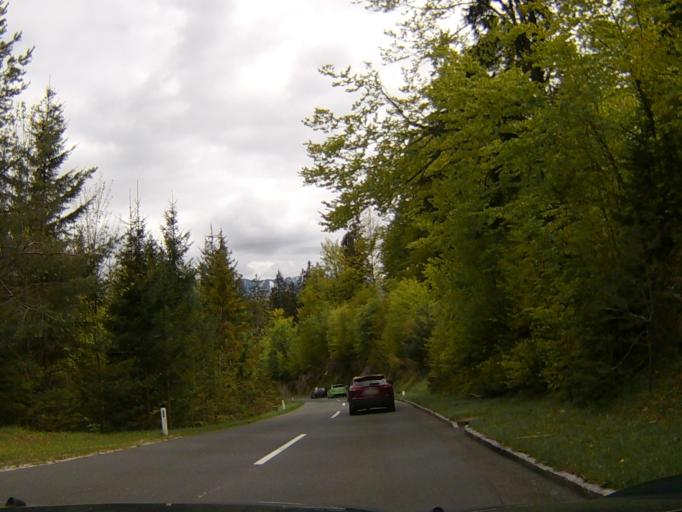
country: AT
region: Carinthia
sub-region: Politischer Bezirk Villach Land
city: Arnoldstein
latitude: 46.5844
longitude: 13.7793
